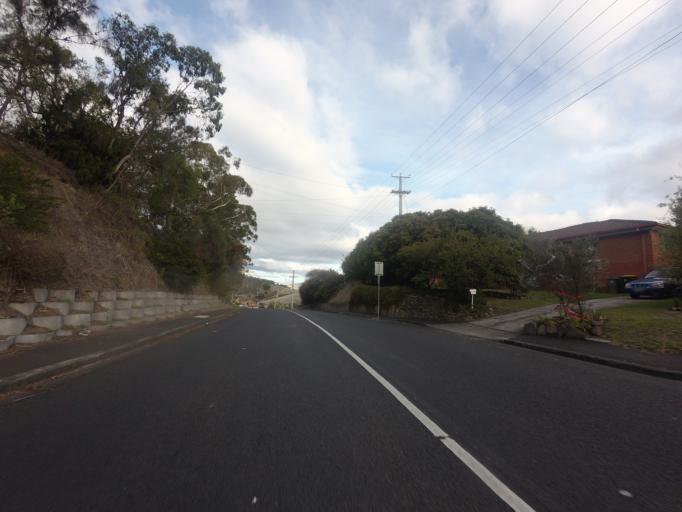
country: AU
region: Tasmania
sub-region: Glenorchy
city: Berriedale
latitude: -42.8199
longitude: 147.2450
